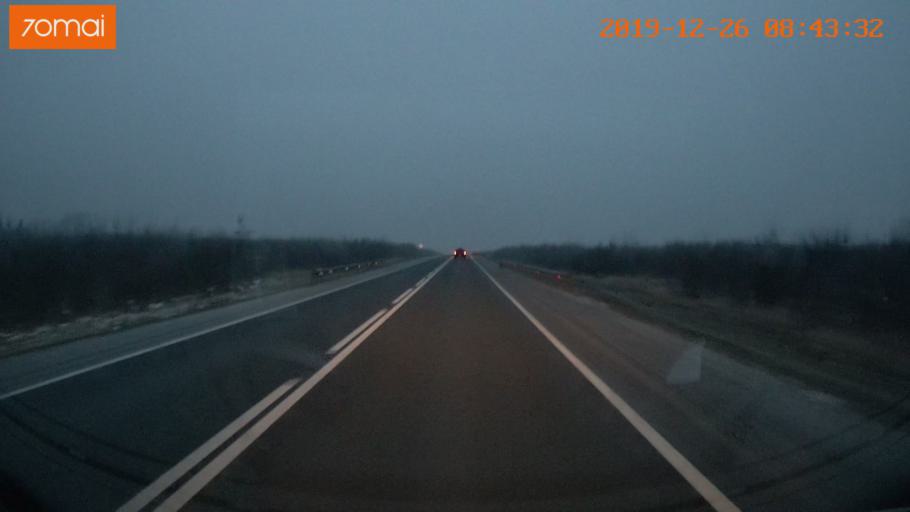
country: RU
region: Jaroslavl
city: Prechistoye
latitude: 58.5742
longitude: 40.3530
